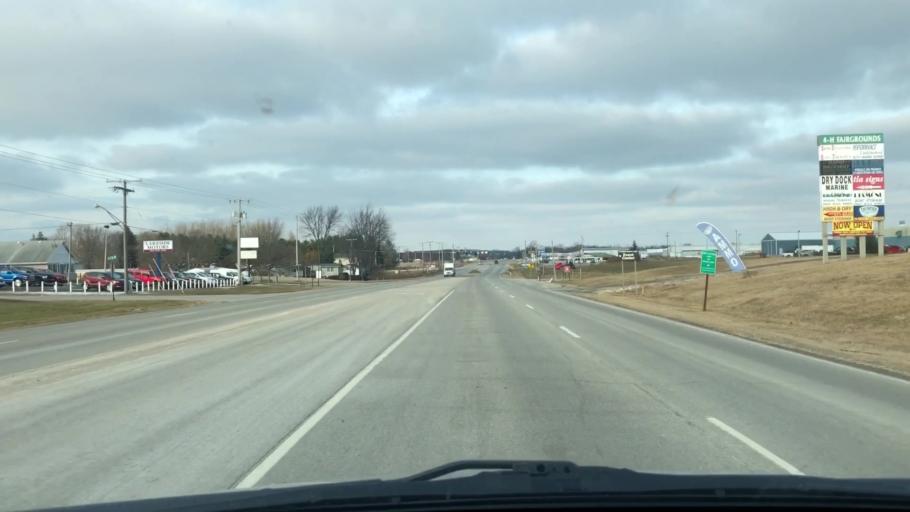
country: US
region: Indiana
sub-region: Steuben County
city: Angola
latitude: 41.6683
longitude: -85.0285
